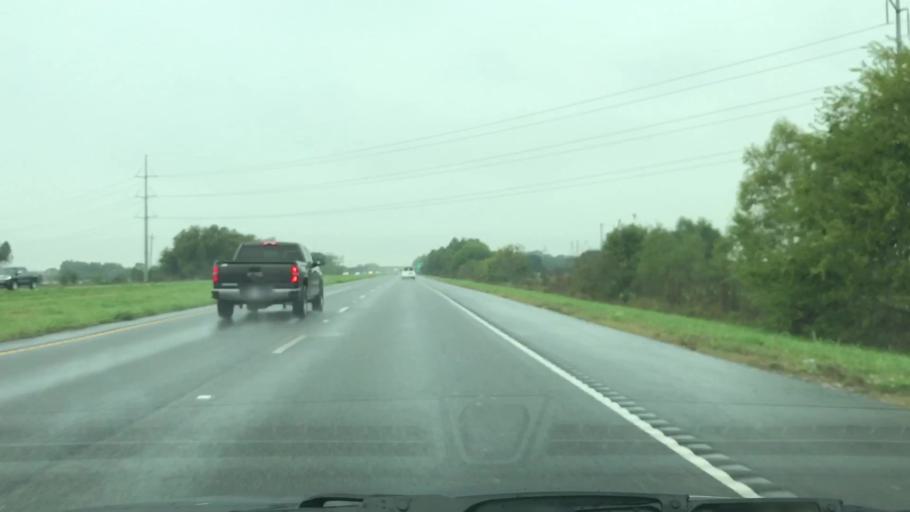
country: US
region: Louisiana
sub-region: Lafourche Parish
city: Raceland
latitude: 29.6901
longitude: -90.6114
